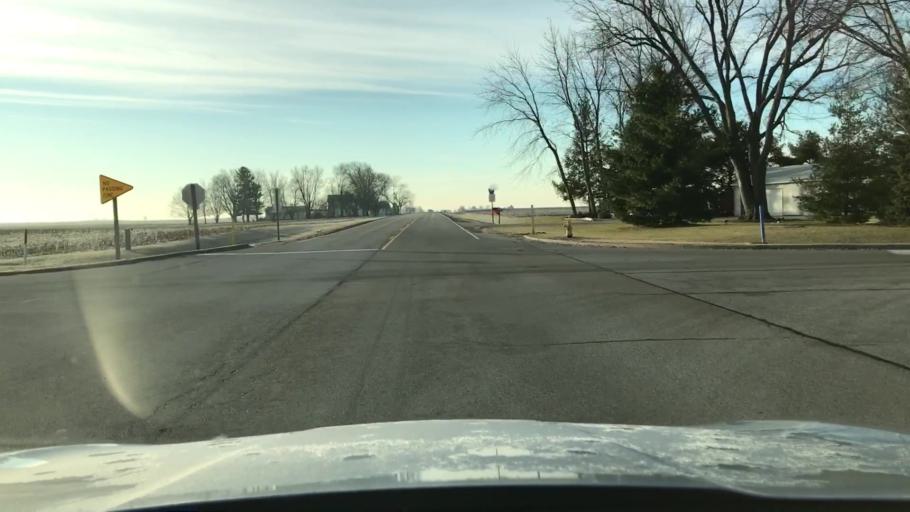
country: US
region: Illinois
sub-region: McLean County
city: Hudson
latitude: 40.6058
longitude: -88.9451
